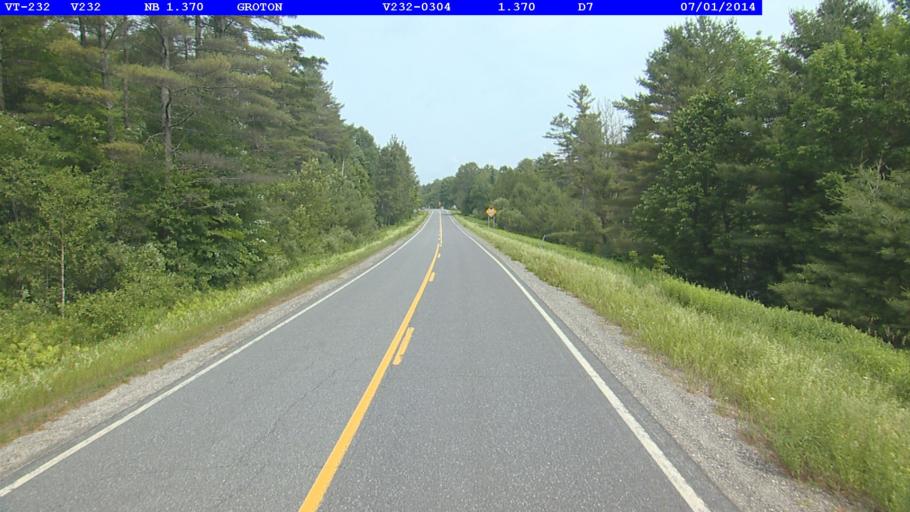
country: US
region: New Hampshire
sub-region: Grafton County
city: Woodsville
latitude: 44.2377
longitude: -72.2356
